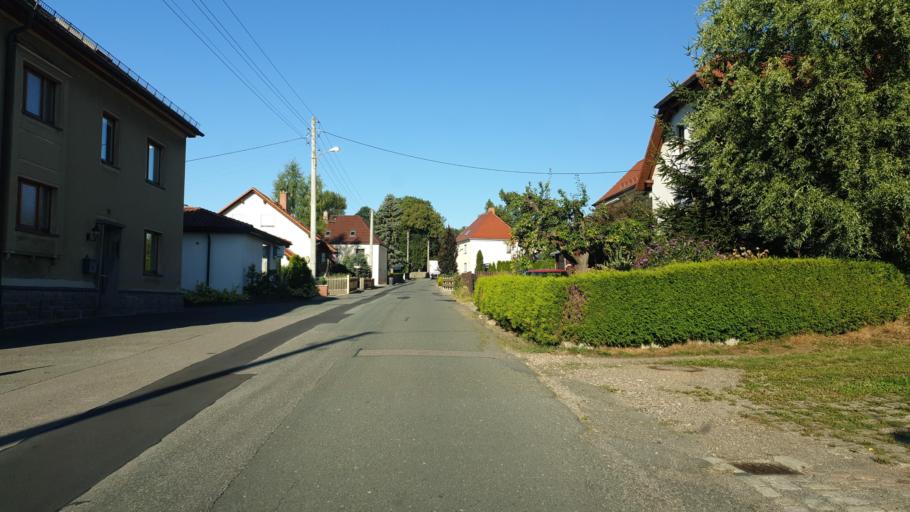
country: DE
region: Saxony
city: Hirschfeld
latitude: 50.6497
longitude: 12.4339
